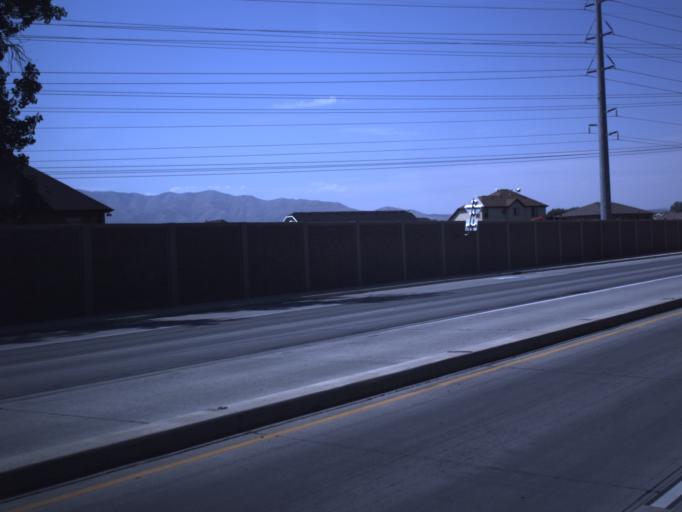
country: US
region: Utah
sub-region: Utah County
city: Lehi
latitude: 40.3739
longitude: -111.8578
